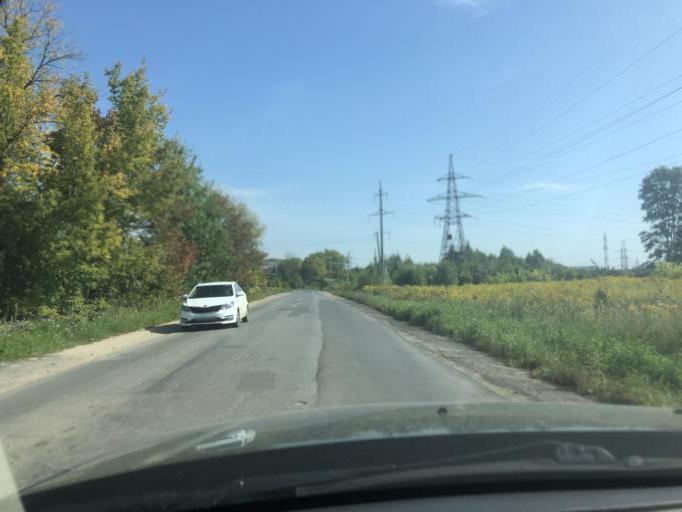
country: RU
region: Tula
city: Mendeleyevskiy
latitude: 54.1251
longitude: 37.6040
